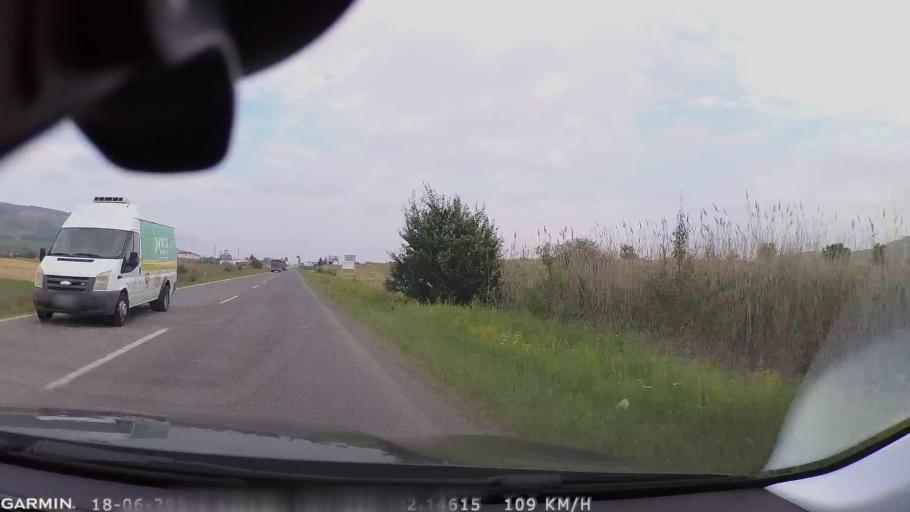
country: MK
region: Stip
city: Shtip
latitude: 41.7714
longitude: 22.1447
